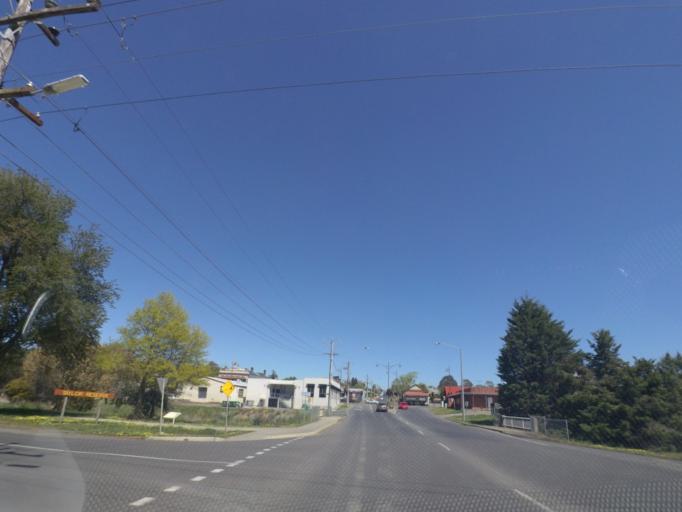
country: AU
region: Victoria
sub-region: Whittlesea
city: Whittlesea
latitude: -37.2907
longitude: 144.9519
